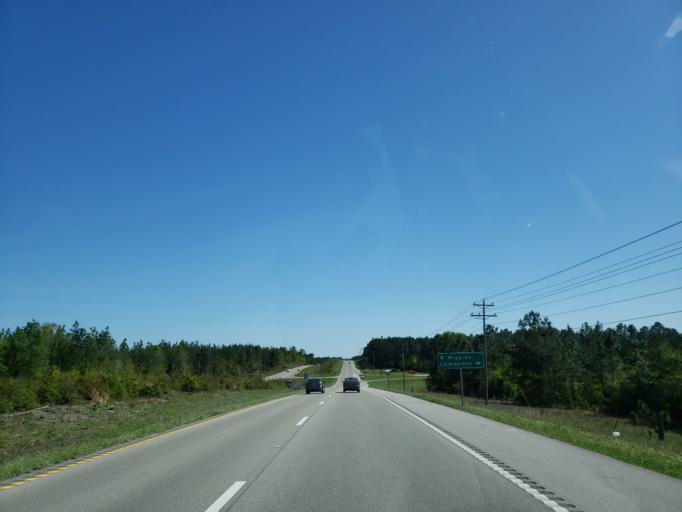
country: US
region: Mississippi
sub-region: Stone County
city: Wiggins
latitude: 30.9529
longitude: -89.1889
